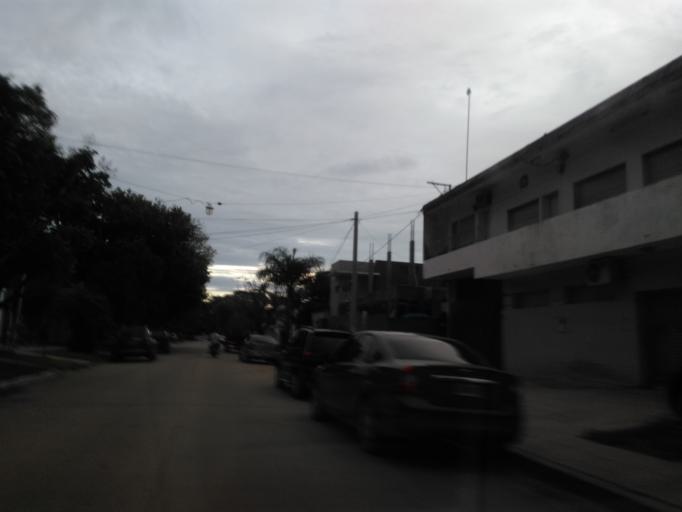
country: AR
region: Chaco
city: Resistencia
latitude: -27.4452
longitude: -58.9736
